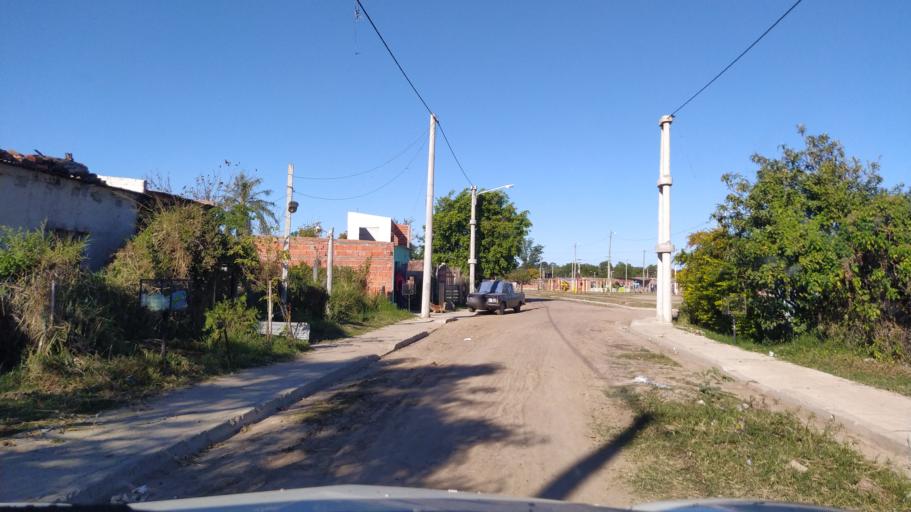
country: AR
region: Corrientes
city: Corrientes
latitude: -27.4966
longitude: -58.8070
